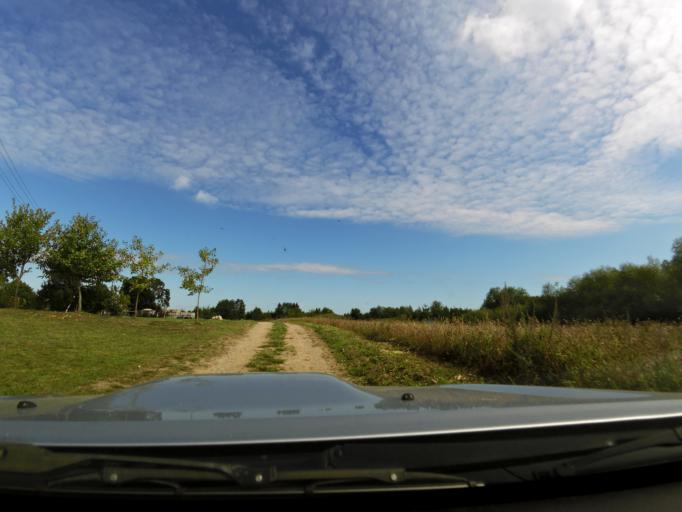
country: LT
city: Grigiskes
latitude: 54.7770
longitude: 25.0133
